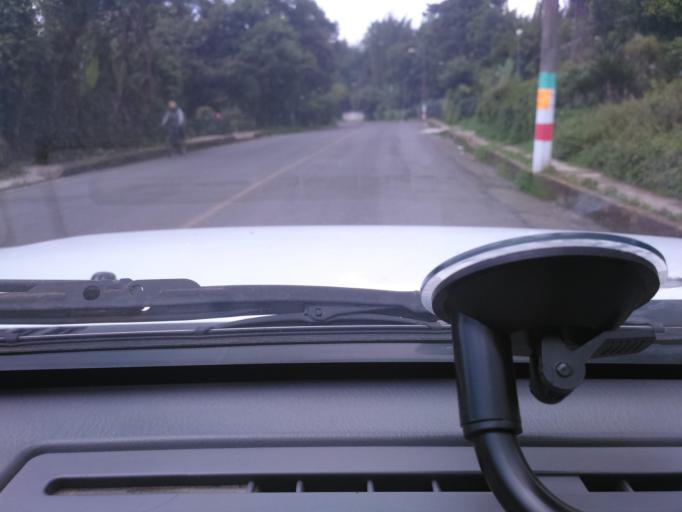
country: MX
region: Veracruz
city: Atzacan
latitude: 18.8960
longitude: -97.0886
